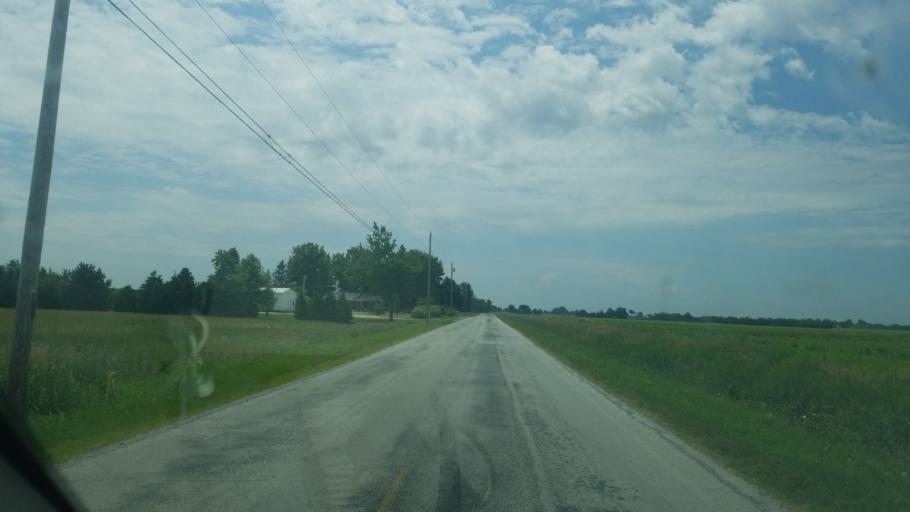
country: US
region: Ohio
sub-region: Wood County
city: Bowling Green
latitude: 41.2801
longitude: -83.5928
